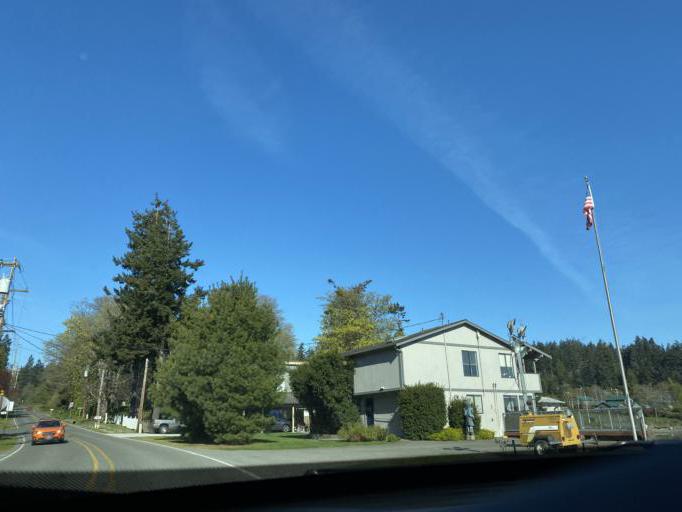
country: US
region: Washington
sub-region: Island County
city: Freeland
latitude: 48.0154
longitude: -122.5401
